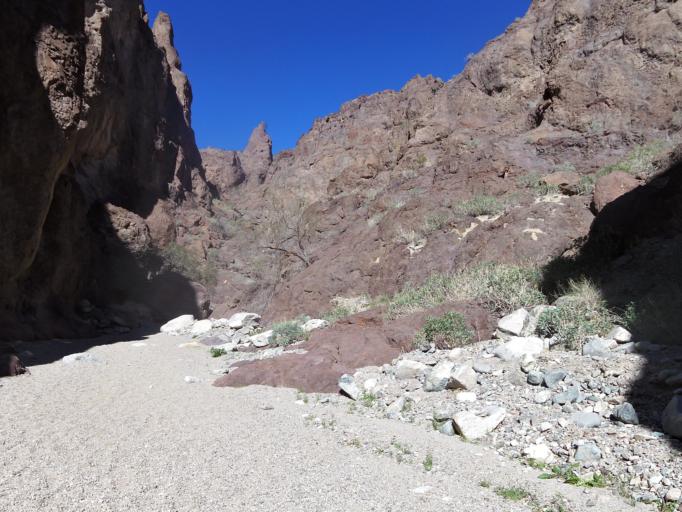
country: US
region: Nevada
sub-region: Clark County
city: Boulder City
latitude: 35.9728
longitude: -114.7168
